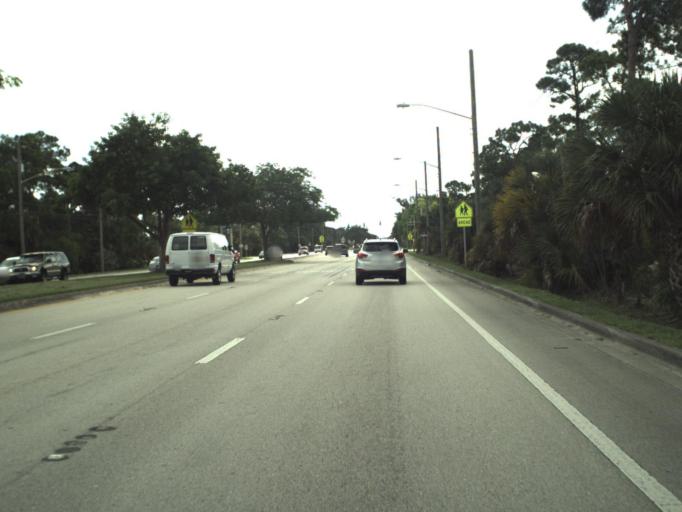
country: US
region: Florida
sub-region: Palm Beach County
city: Greenacres City
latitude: 26.6510
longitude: -80.1594
